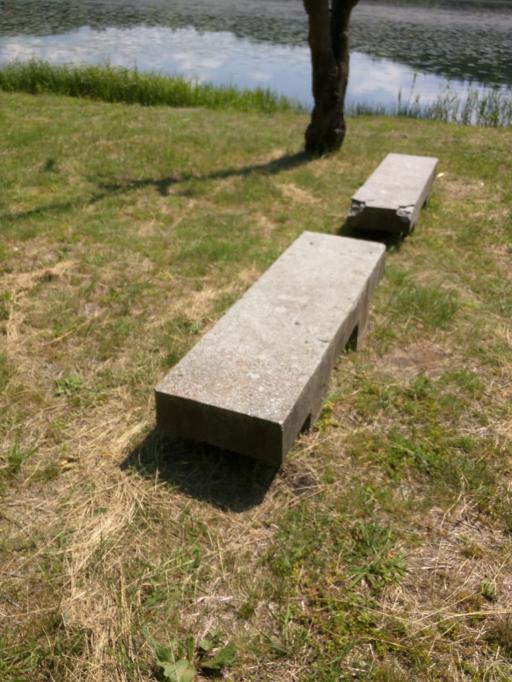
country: JP
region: Tochigi
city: Kuroiso
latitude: 37.1107
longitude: 140.2151
